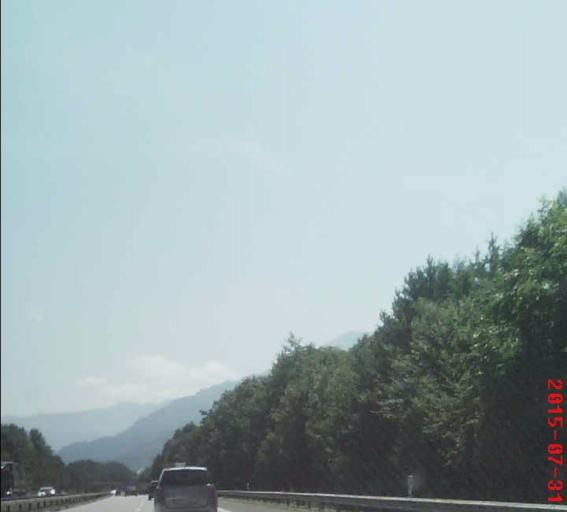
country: LI
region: Gamprin
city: Gamprin
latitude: 47.2194
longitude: 9.4995
